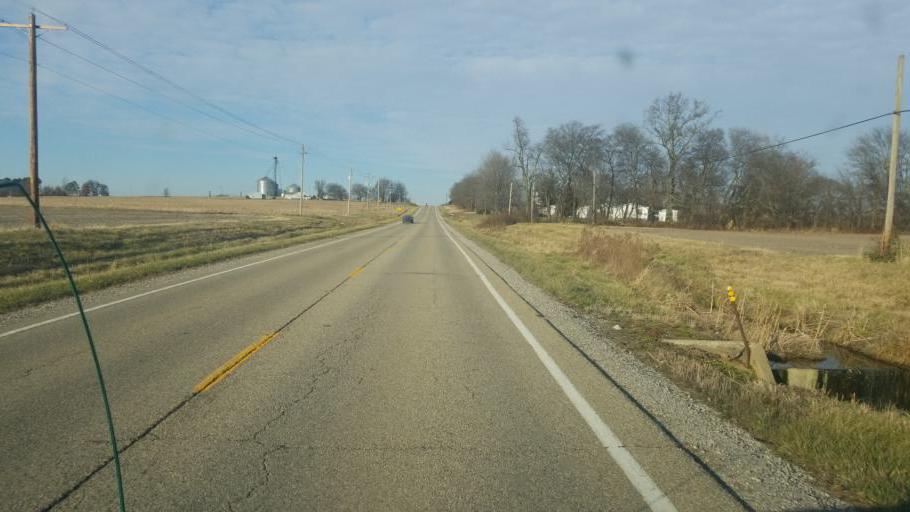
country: US
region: Illinois
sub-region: Lawrence County
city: Lawrenceville
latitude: 38.6529
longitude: -87.6943
